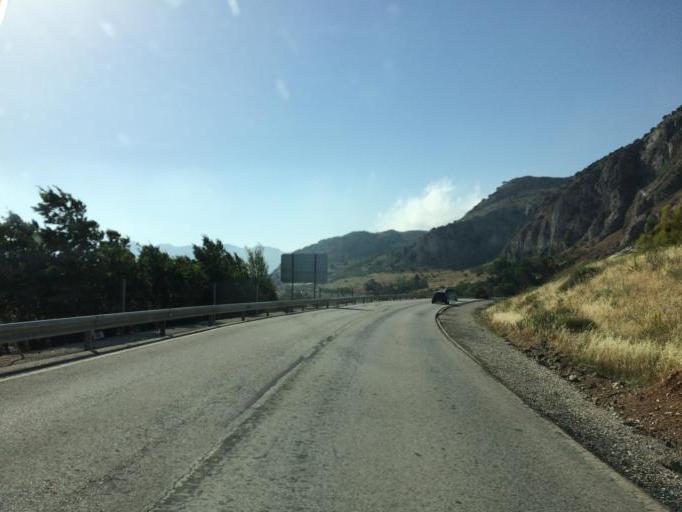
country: ES
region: Andalusia
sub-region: Provincia de Malaga
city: Casabermeja
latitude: 36.9843
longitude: -4.4622
